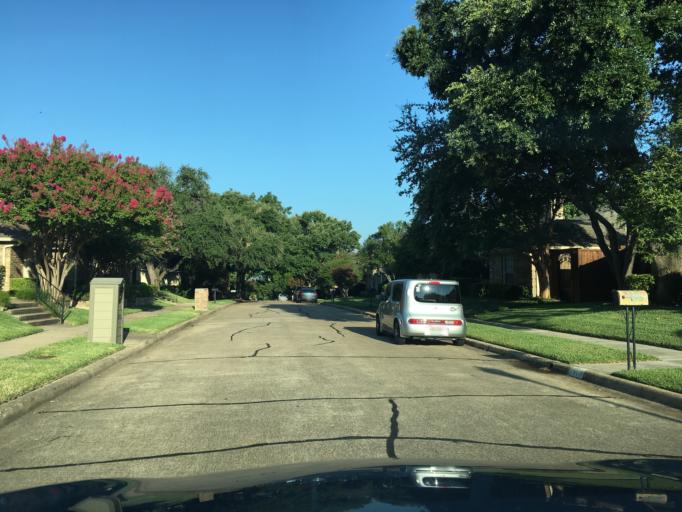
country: US
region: Texas
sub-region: Dallas County
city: Addison
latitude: 32.9684
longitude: -96.8559
